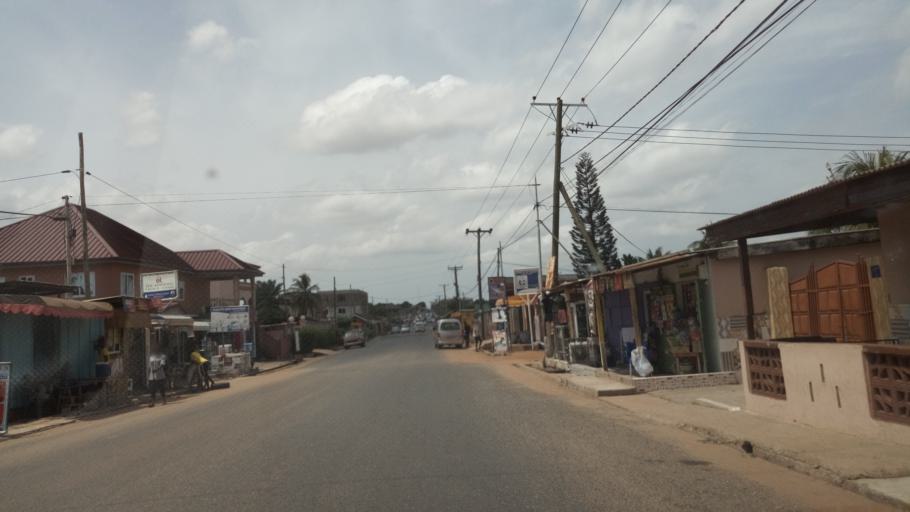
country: GH
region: Greater Accra
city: Medina Estates
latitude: 5.6835
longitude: -0.1605
